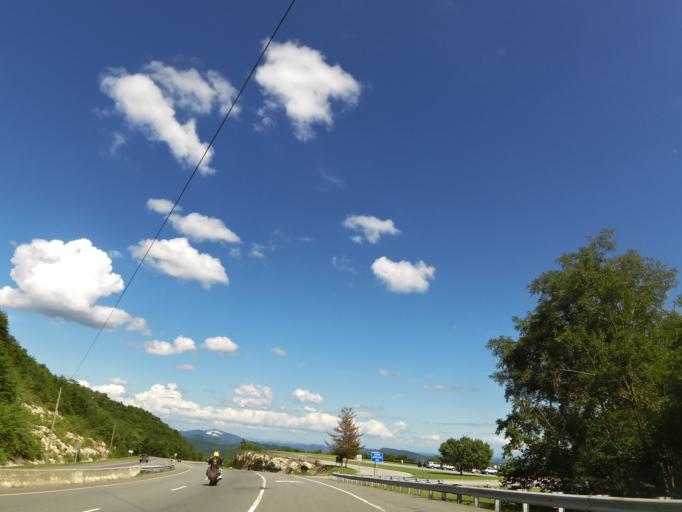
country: US
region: Tennessee
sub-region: Grainger County
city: Bean Station
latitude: 36.3501
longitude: -83.3953
